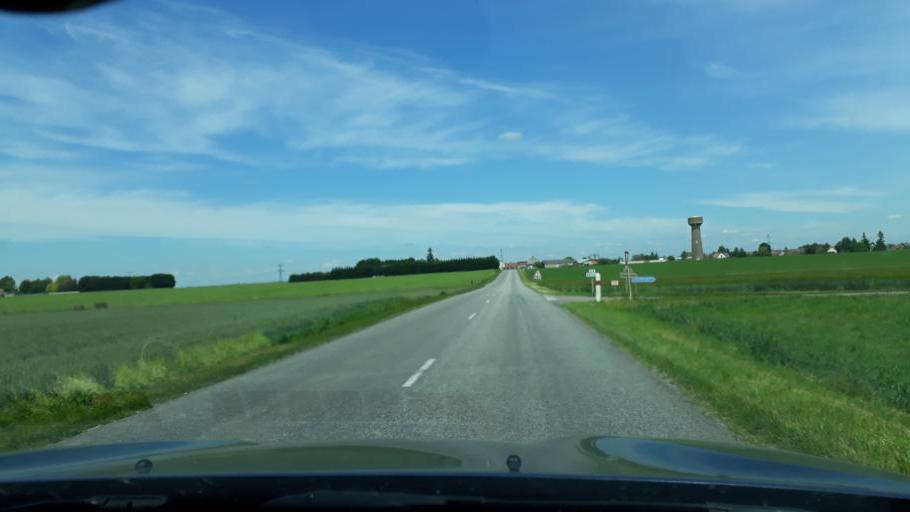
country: FR
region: Centre
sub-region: Departement du Loiret
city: Dadonville
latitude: 48.0965
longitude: 2.2702
